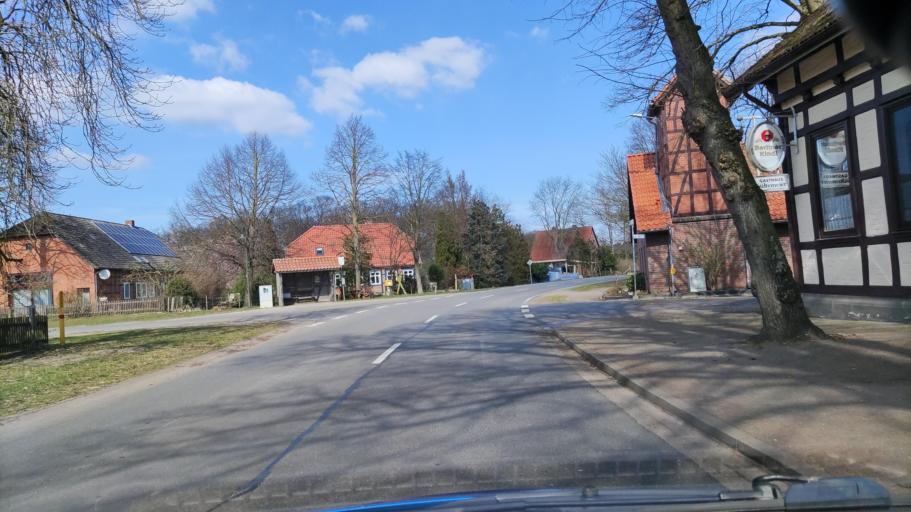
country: DE
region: Lower Saxony
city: Trebel
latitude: 53.0270
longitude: 11.2668
